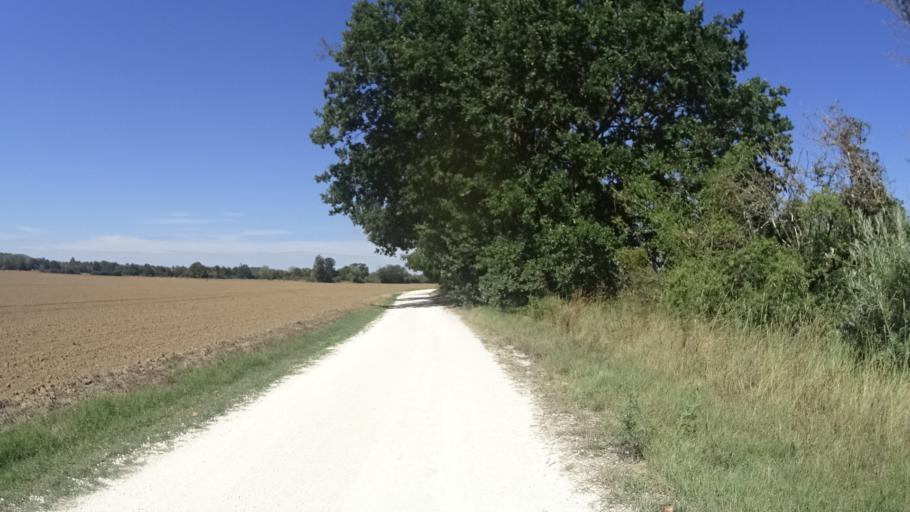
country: FR
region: Bourgogne
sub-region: Departement de la Nievre
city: Neuvy-sur-Loire
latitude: 47.5290
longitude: 2.8568
